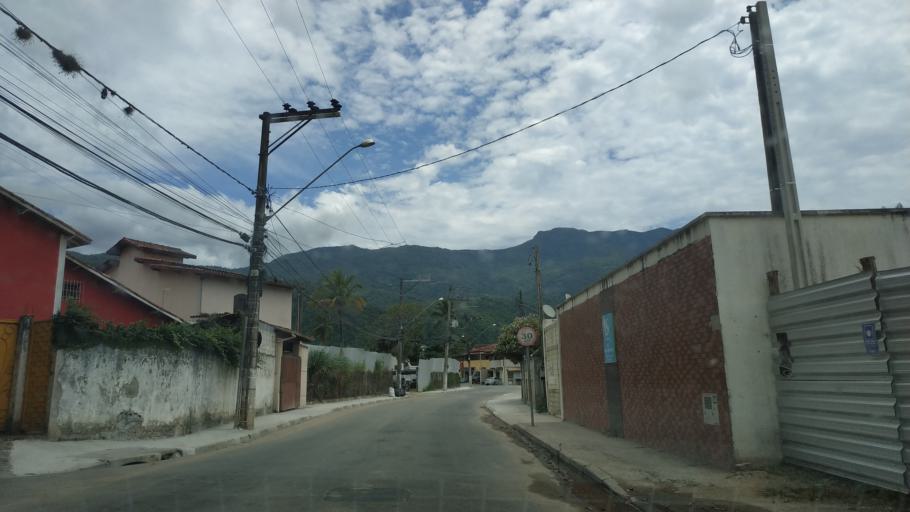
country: BR
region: Sao Paulo
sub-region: Ilhabela
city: Ilhabela
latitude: -23.8206
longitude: -45.3613
